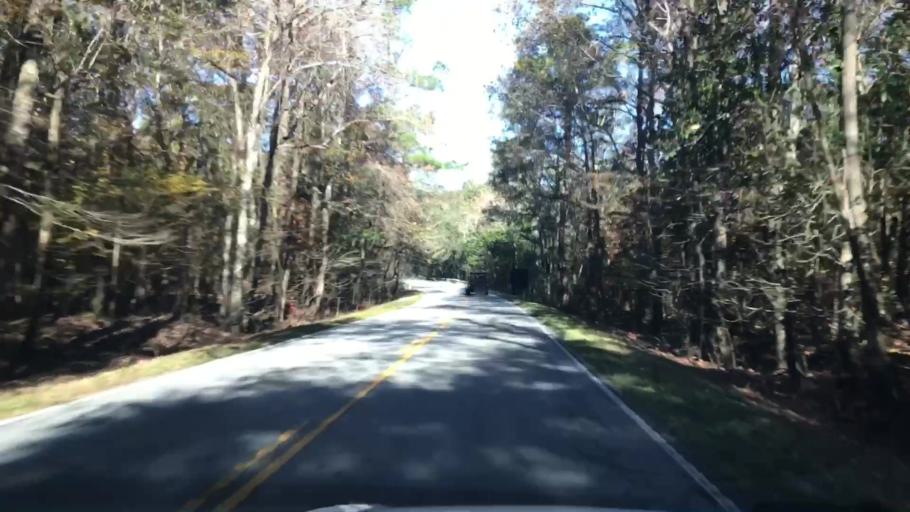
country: US
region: South Carolina
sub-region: Berkeley County
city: Ladson
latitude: 32.9088
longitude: -80.1486
